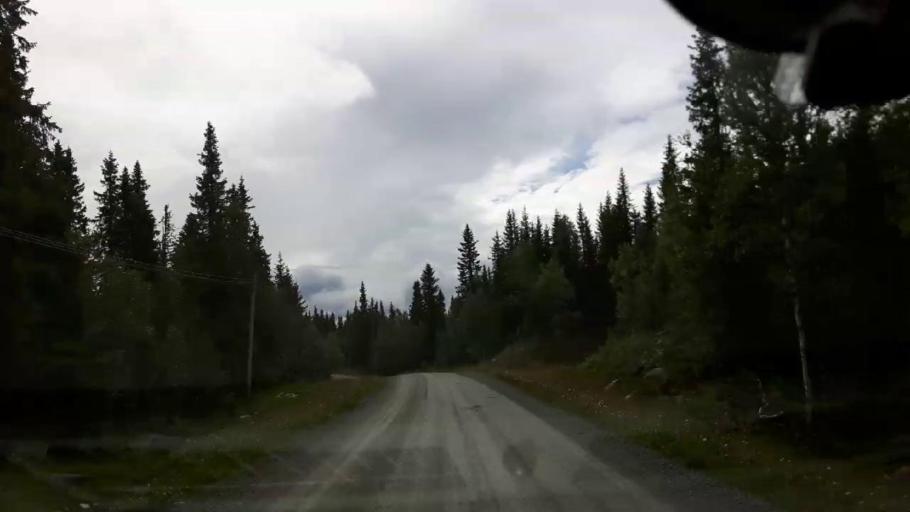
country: SE
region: Jaemtland
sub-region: Krokoms Kommun
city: Valla
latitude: 63.7325
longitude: 13.8356
